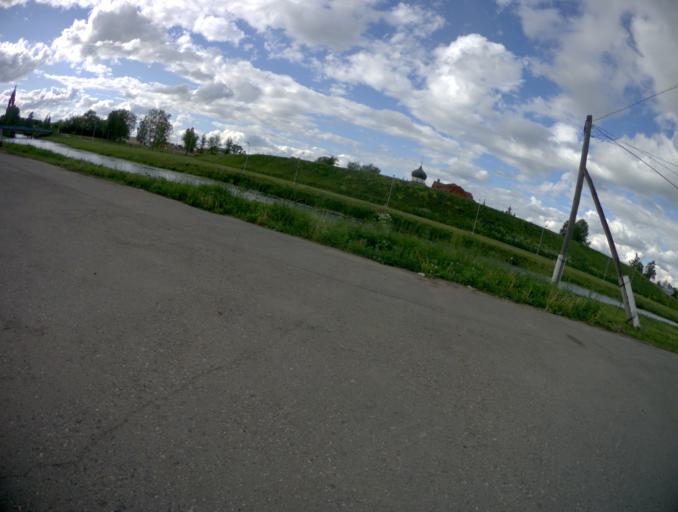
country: RU
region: Vladimir
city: Yur'yev-Pol'skiy
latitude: 56.4950
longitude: 39.6796
